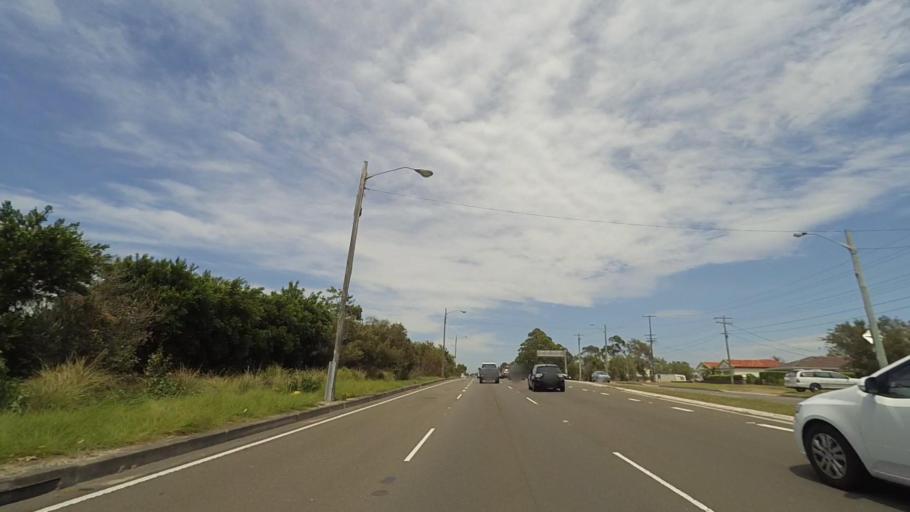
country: AU
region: New South Wales
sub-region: Sutherland Shire
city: Heathcote
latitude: -34.0919
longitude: 151.0030
